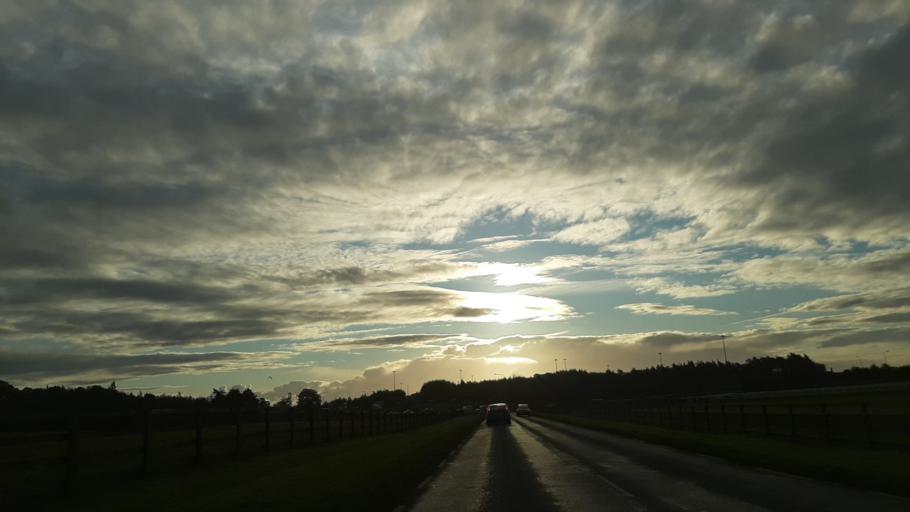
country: IE
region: Leinster
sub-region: Kildare
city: Athgarvan
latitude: 53.1642
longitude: -6.8318
